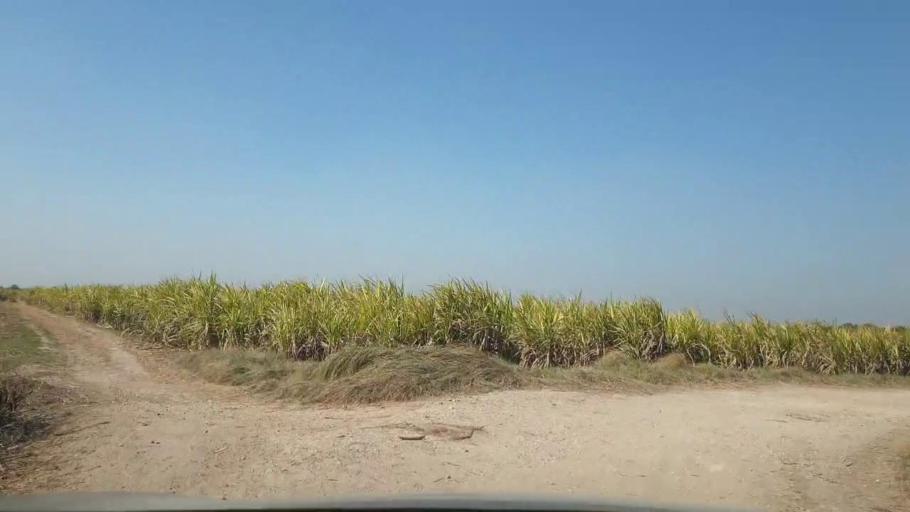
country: PK
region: Sindh
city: Tando Adam
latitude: 25.6328
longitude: 68.6750
